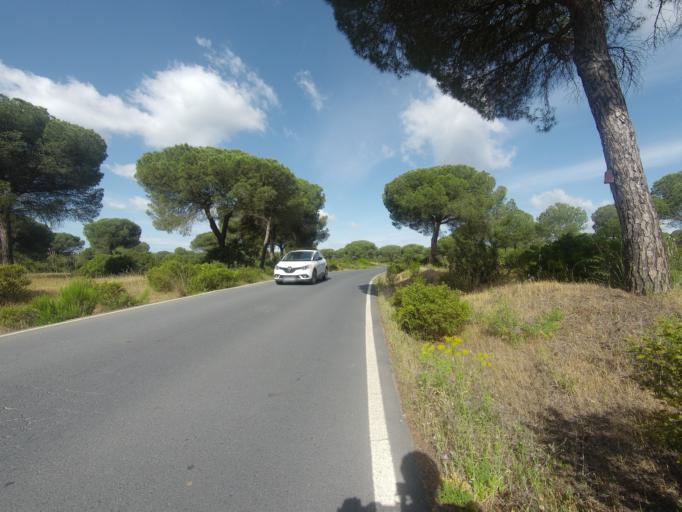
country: ES
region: Andalusia
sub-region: Provincia de Huelva
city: Aljaraque
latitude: 37.2472
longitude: -7.0245
